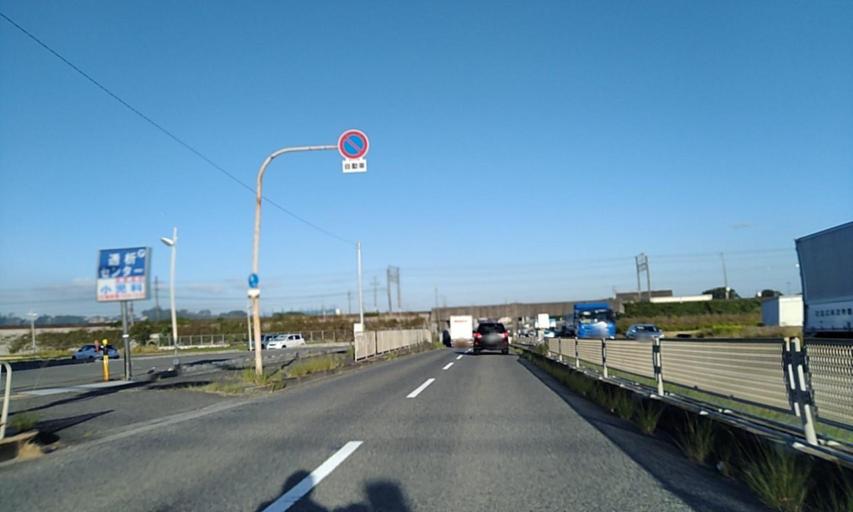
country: JP
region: Wakayama
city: Iwade
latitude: 34.3487
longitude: 135.2708
